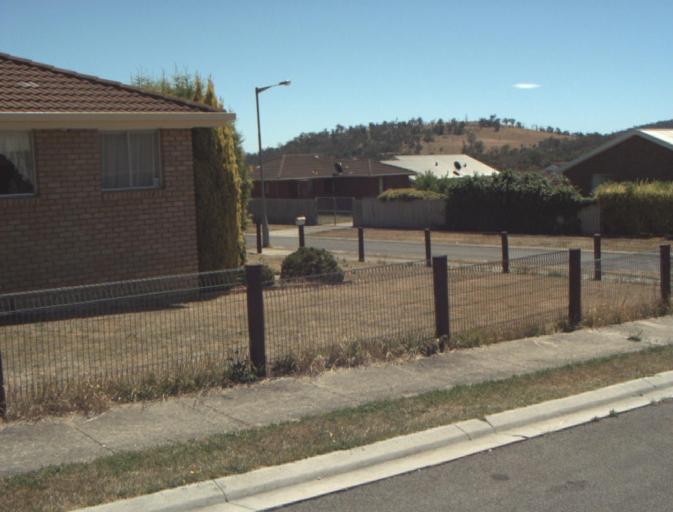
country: AU
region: Tasmania
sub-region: Launceston
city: Mayfield
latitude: -41.3751
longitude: 147.1402
